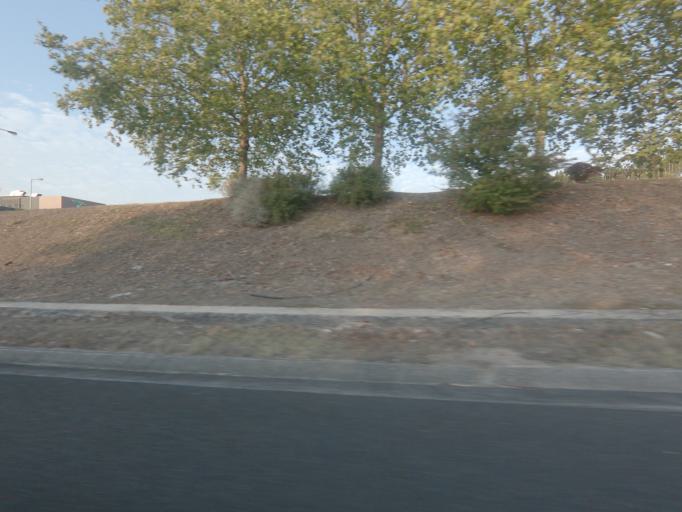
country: PT
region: Leiria
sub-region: Leiria
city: Caranguejeira
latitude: 39.7130
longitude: -8.7105
